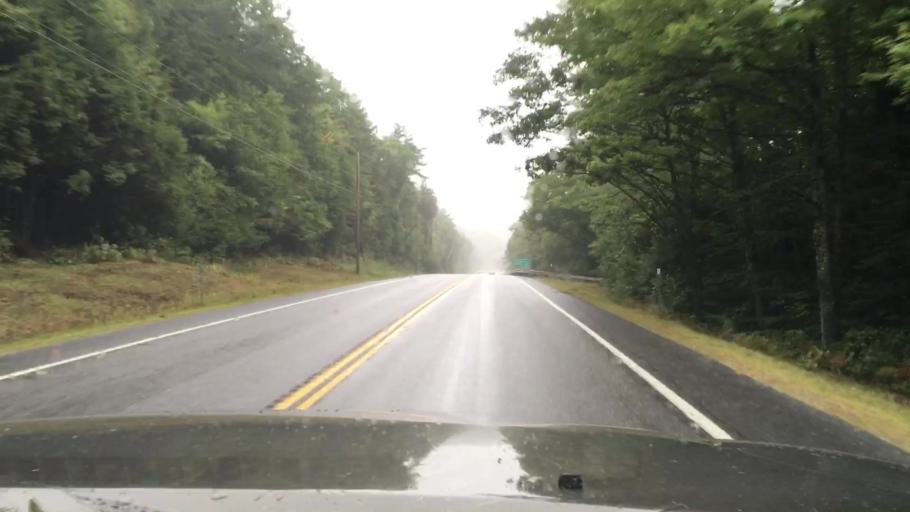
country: US
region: New Hampshire
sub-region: Cheshire County
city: Harrisville
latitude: 43.0292
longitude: -72.1208
